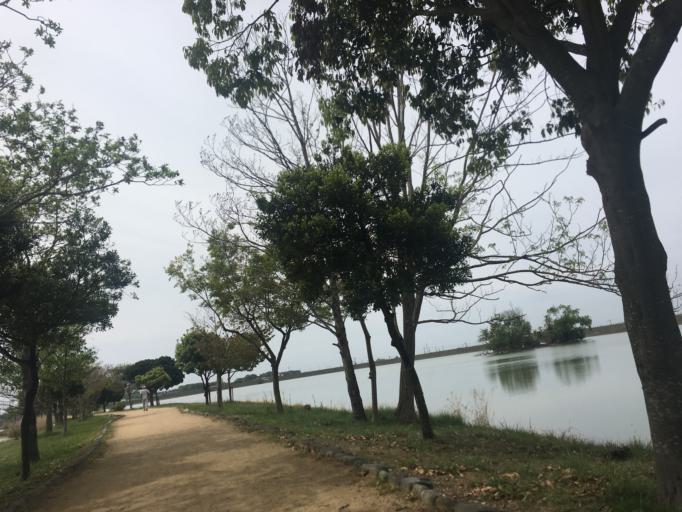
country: JP
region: Hyogo
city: Miki
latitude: 34.7664
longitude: 134.9228
